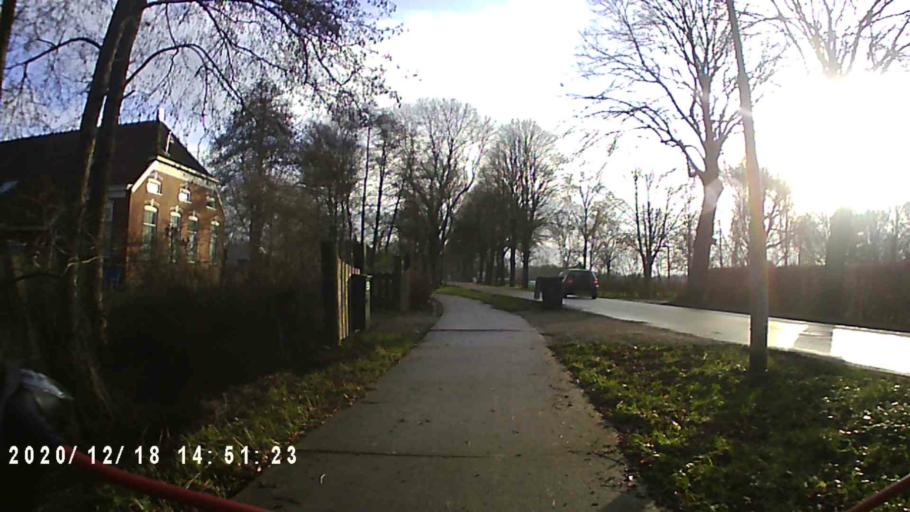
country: NL
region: Groningen
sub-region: Gemeente Haren
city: Haren
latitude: 53.1951
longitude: 6.6747
